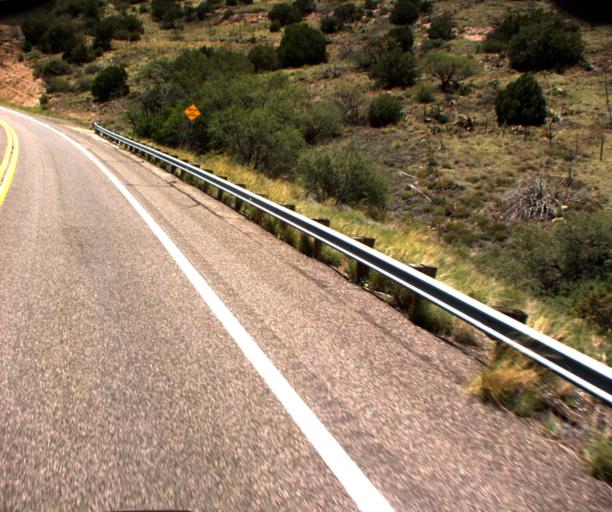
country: US
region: Arizona
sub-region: Yavapai County
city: Lake Montezuma
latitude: 34.5060
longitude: -111.6689
